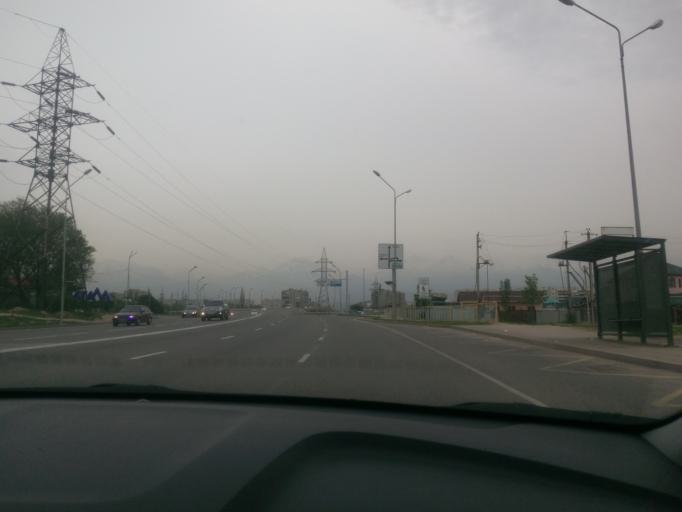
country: KZ
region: Almaty Qalasy
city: Almaty
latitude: 43.2485
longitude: 76.8253
